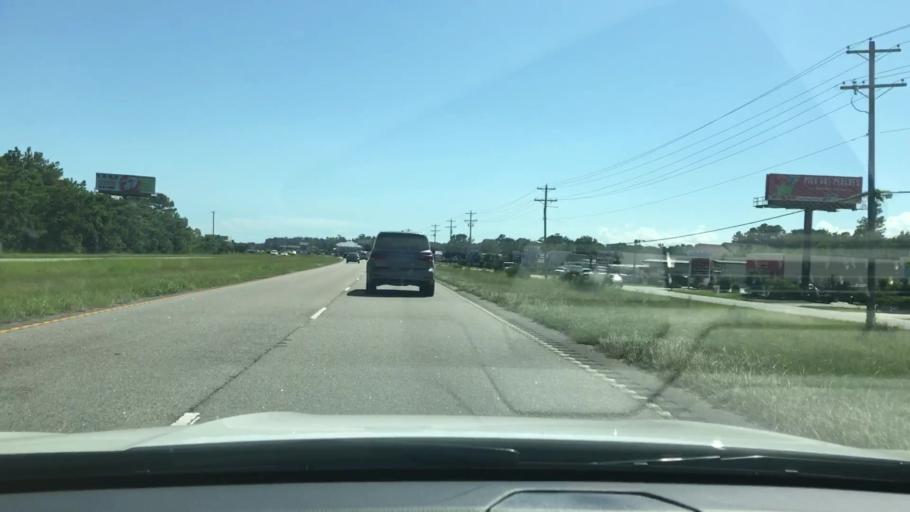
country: US
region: South Carolina
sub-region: Horry County
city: Garden City
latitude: 33.5925
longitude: -79.0253
